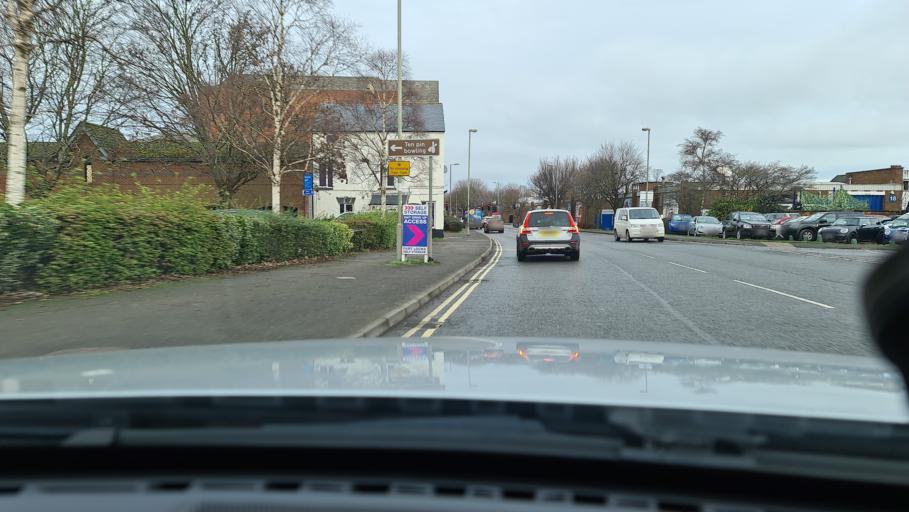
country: GB
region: England
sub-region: Oxfordshire
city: Banbury
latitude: 52.0590
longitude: -1.3321
